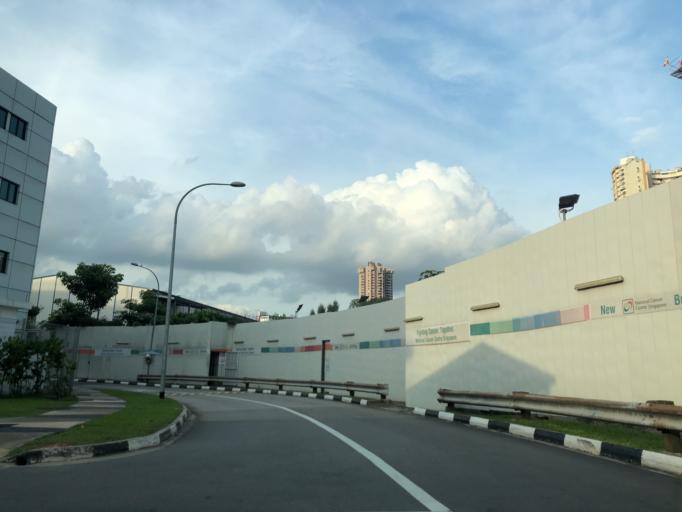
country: SG
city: Singapore
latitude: 1.2809
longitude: 103.8372
